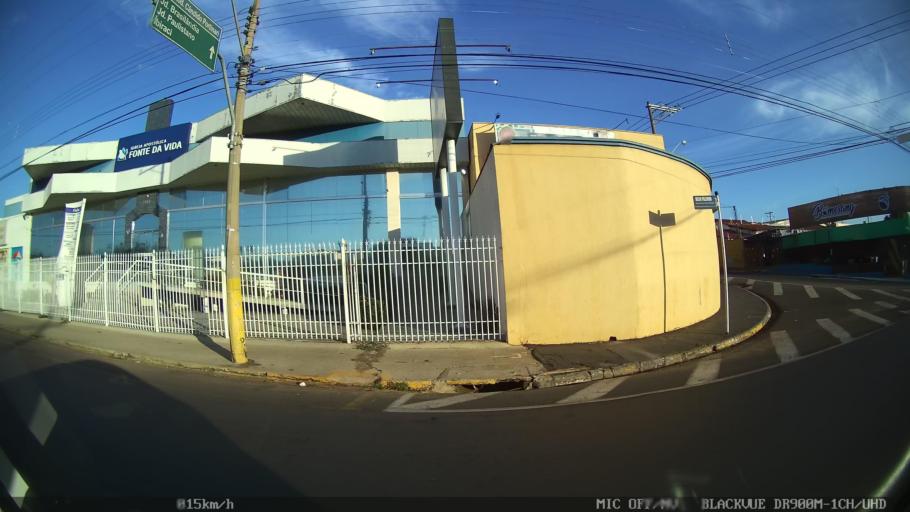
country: BR
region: Sao Paulo
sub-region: Franca
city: Franca
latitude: -20.5202
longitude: -47.3970
